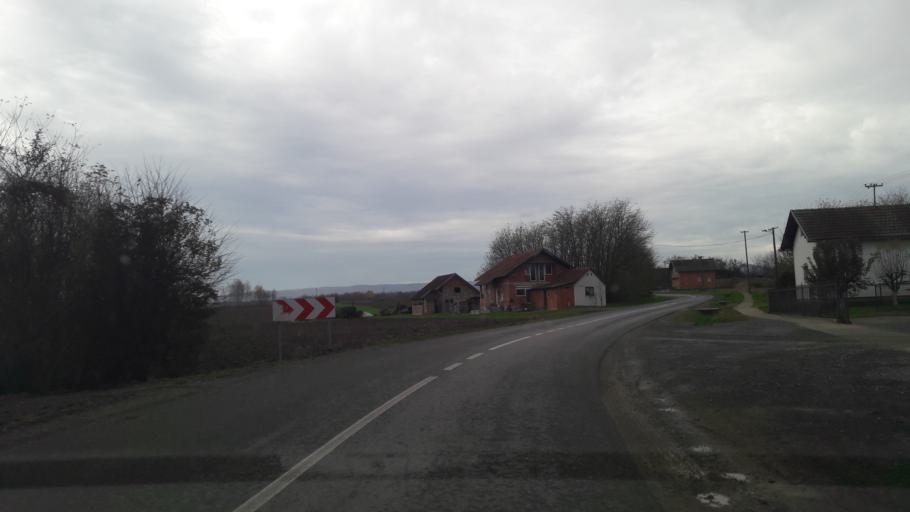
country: HR
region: Osjecko-Baranjska
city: Fericanci
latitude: 45.5240
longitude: 18.0130
